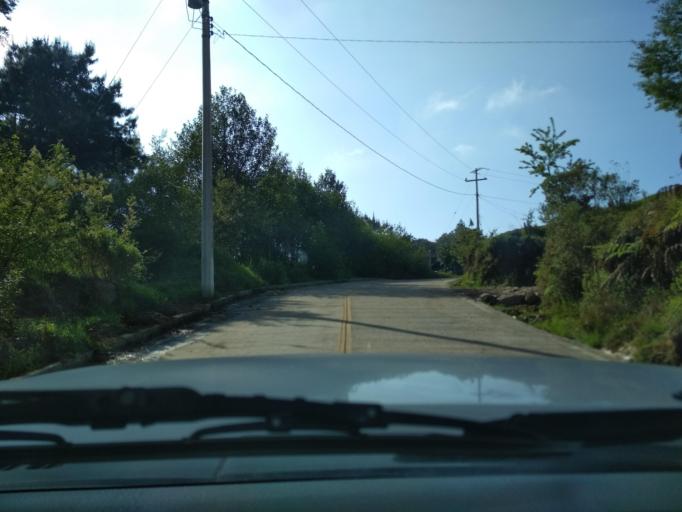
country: MX
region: Veracruz
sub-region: La Perla
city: Chilapa
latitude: 19.0037
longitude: -97.1823
